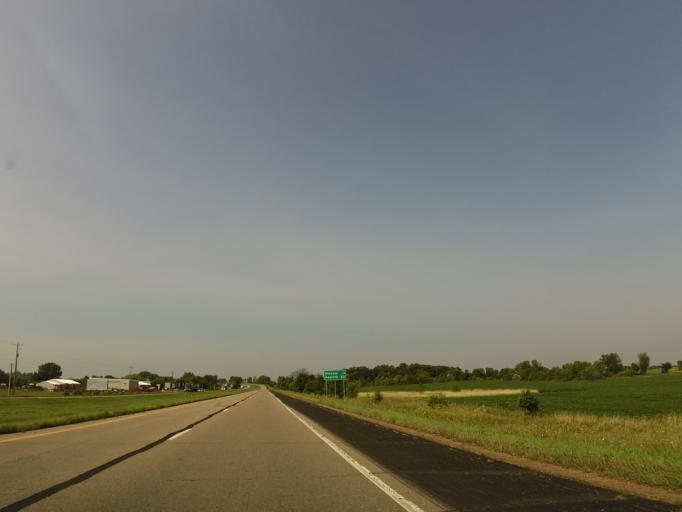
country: US
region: Minnesota
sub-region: Carver County
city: Norwood (historical)
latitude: 44.7720
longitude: -93.9368
